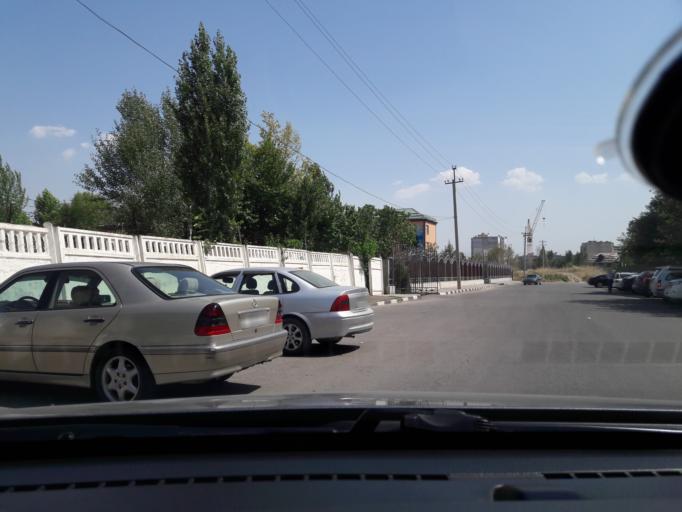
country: TJ
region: Dushanbe
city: Dushanbe
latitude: 38.5763
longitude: 68.7490
